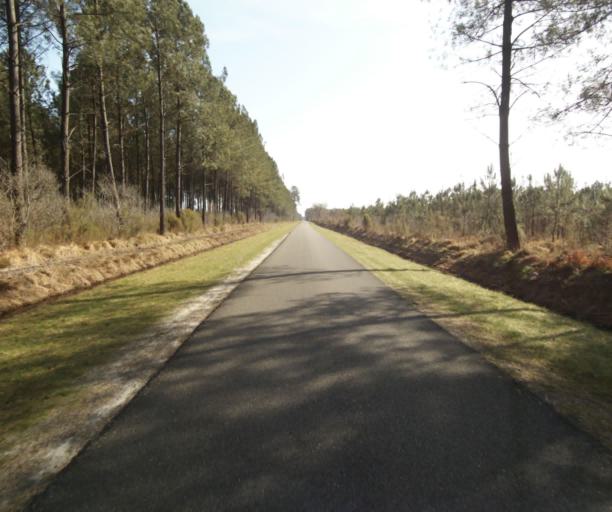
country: FR
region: Aquitaine
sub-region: Departement de la Gironde
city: Grignols
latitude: 44.2300
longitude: -0.1530
